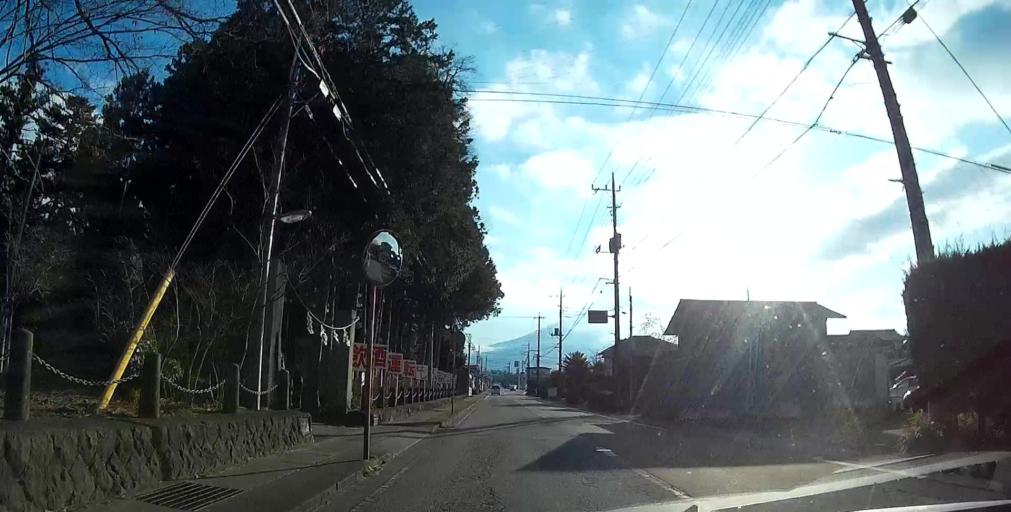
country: JP
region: Yamanashi
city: Fujikawaguchiko
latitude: 35.4845
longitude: 138.8188
